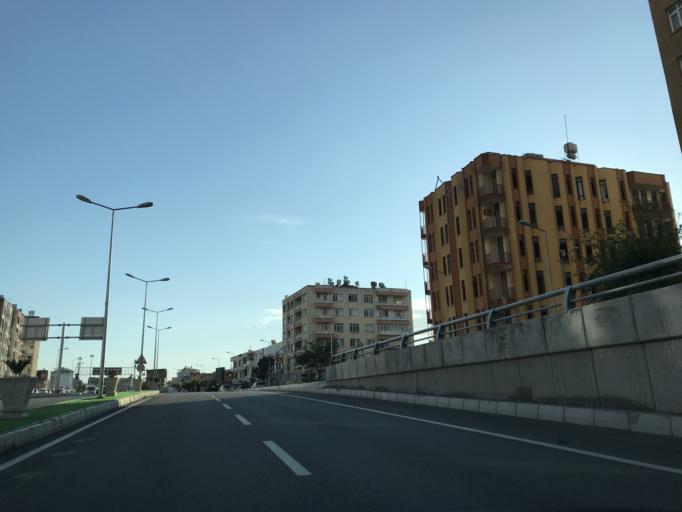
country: TR
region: Hatay
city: Iskenderun
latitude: 36.5817
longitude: 36.1659
